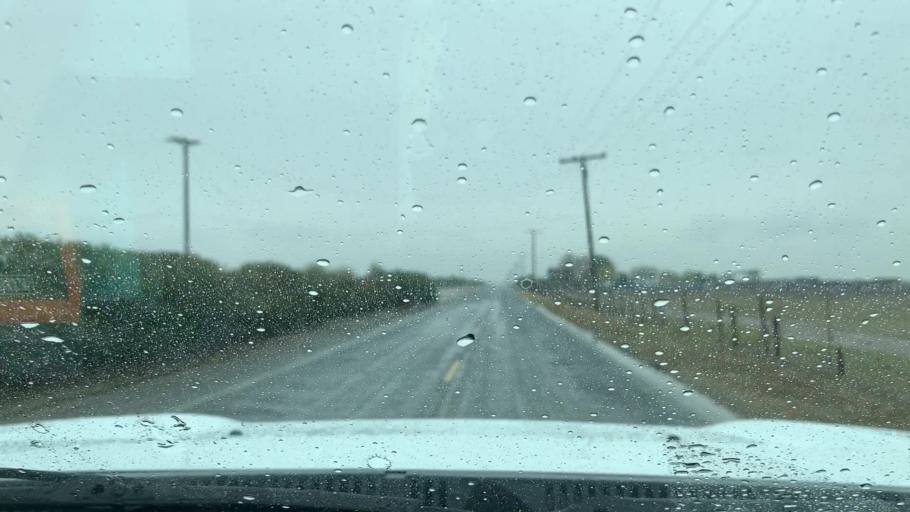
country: US
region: California
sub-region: Tulare County
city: Earlimart
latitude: 35.8919
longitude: -119.3405
